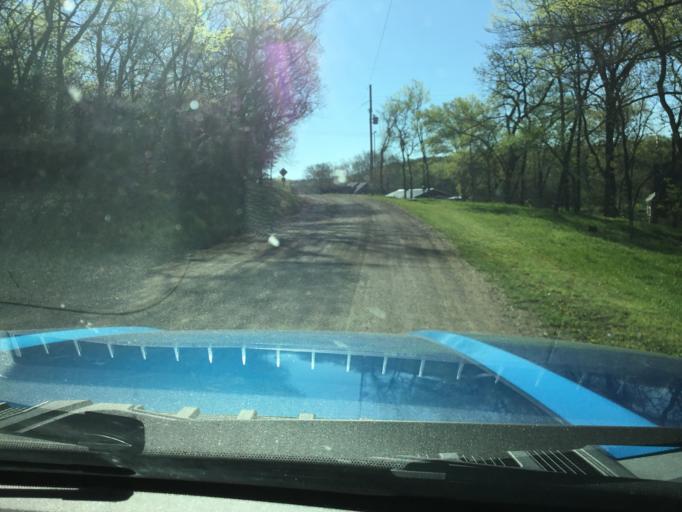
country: US
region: Kansas
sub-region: Douglas County
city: Lawrence
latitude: 38.9930
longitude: -95.3395
